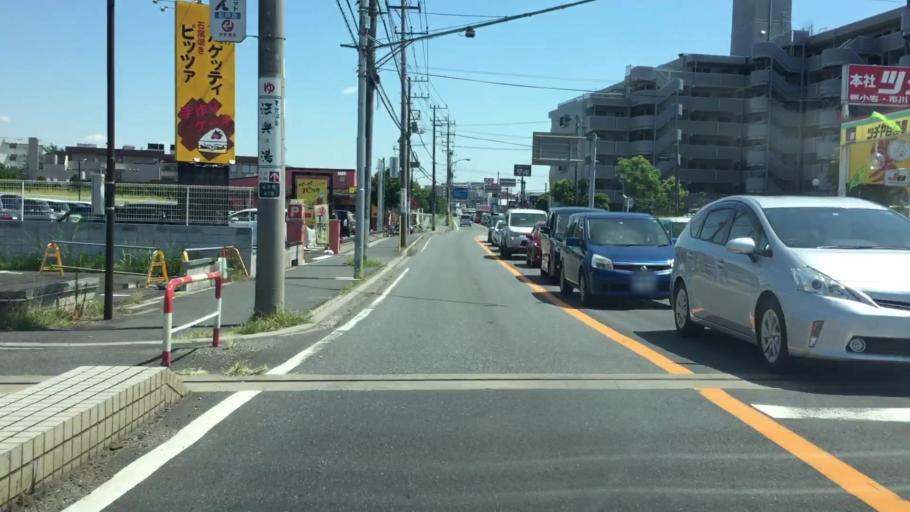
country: JP
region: Chiba
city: Funabashi
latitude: 35.7388
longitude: 139.9522
